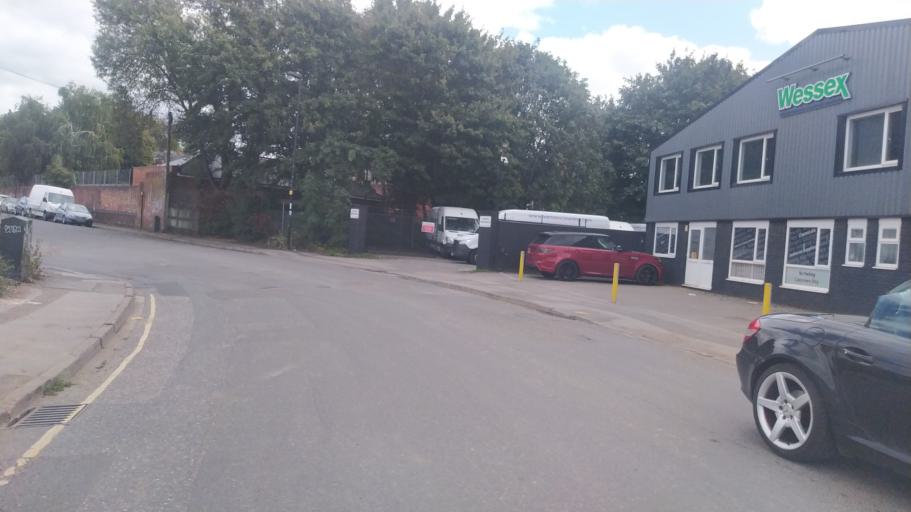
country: GB
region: England
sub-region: Southampton
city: Southampton
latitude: 50.9159
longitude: -1.3948
